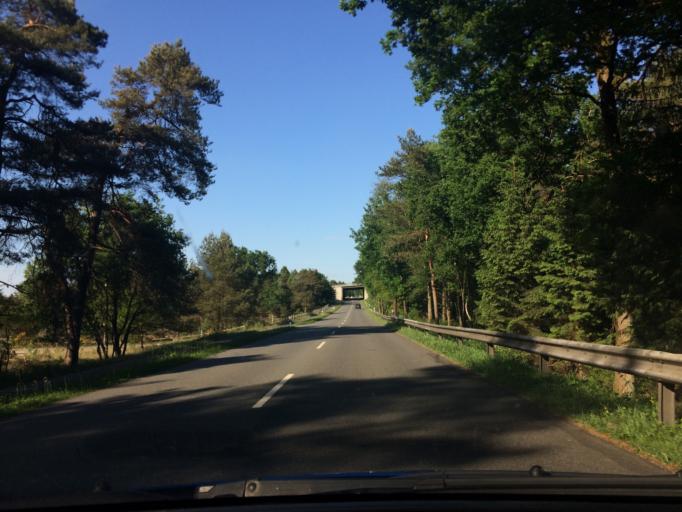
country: DE
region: Lower Saxony
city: Bispingen
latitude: 53.0565
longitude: 9.9509
